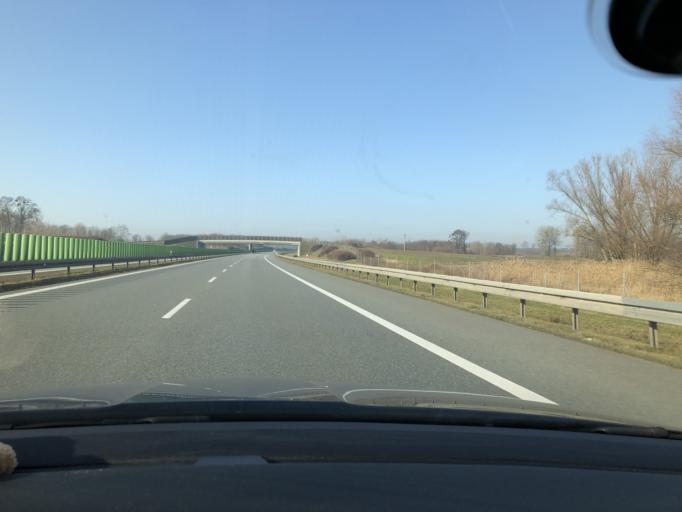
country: PL
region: Greater Poland Voivodeship
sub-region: Powiat poznanski
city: Dopiewo
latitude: 52.3550
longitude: 16.6275
